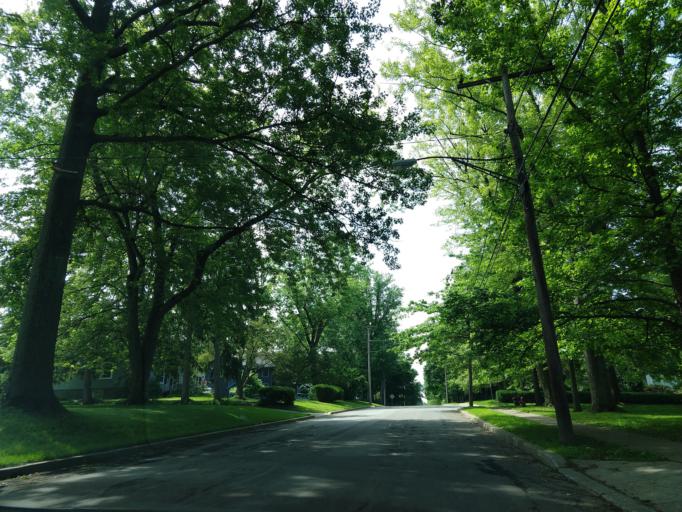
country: US
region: New York
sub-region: Erie County
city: East Aurora
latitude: 42.7659
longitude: -78.6020
